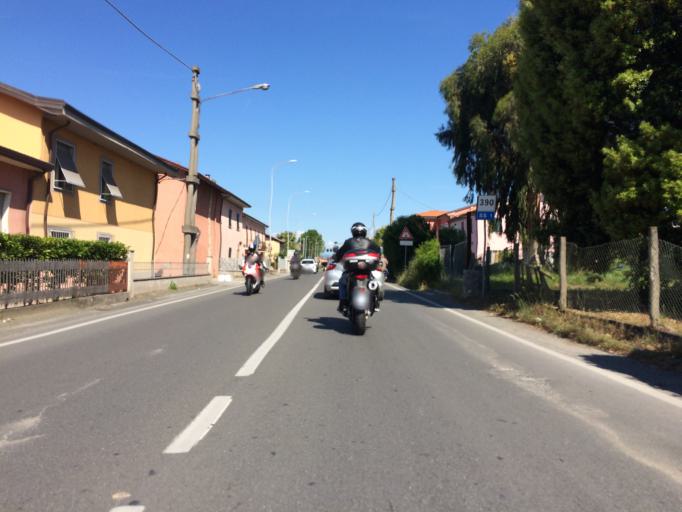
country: IT
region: Liguria
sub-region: Provincia di La Spezia
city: Casano-Dogana-Isola
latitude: 44.0713
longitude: 10.0229
